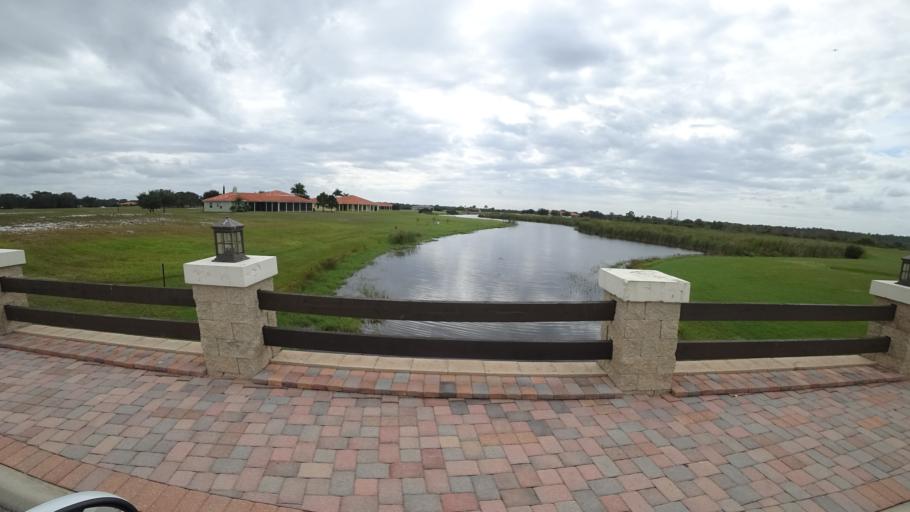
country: US
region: Florida
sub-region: Hillsborough County
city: Wimauma
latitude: 27.6535
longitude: -82.3310
